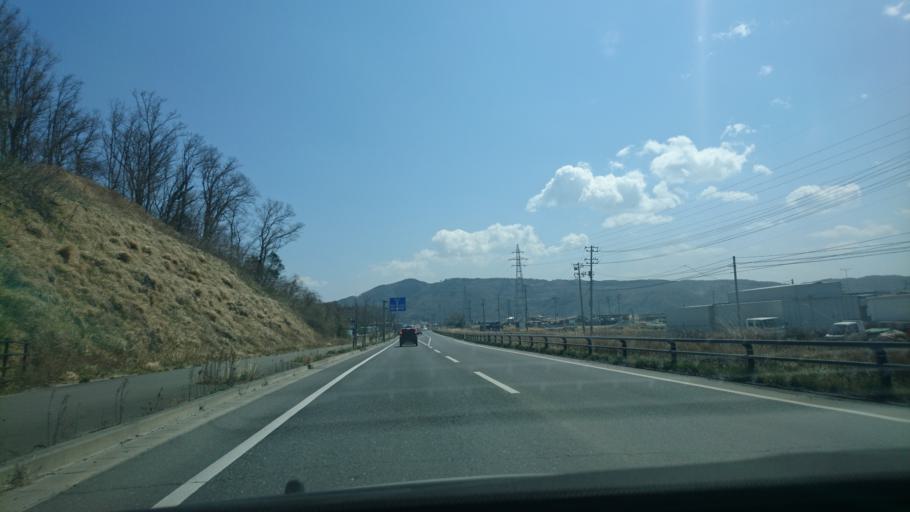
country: JP
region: Miyagi
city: Ishinomaki
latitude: 38.4538
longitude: 141.3102
